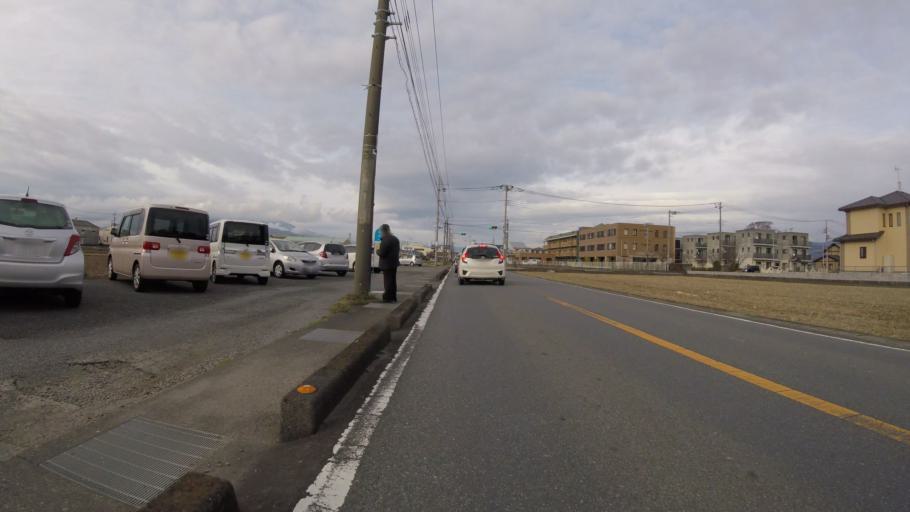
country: JP
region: Shizuoka
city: Mishima
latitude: 35.0964
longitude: 138.9117
